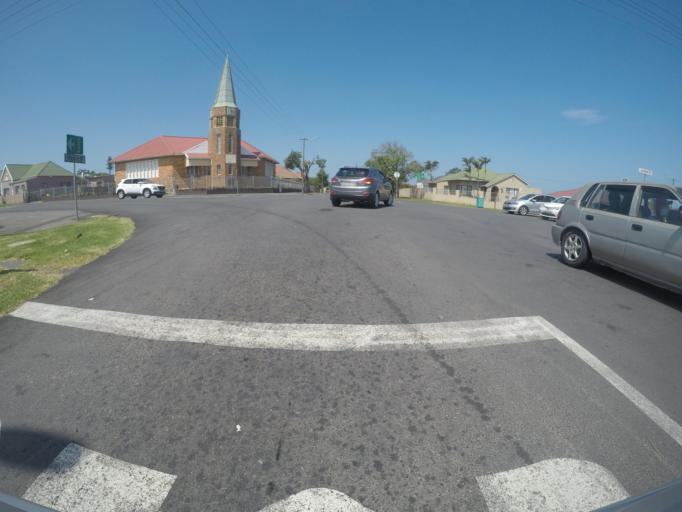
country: ZA
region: Eastern Cape
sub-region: Buffalo City Metropolitan Municipality
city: East London
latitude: -32.9789
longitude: 27.8852
